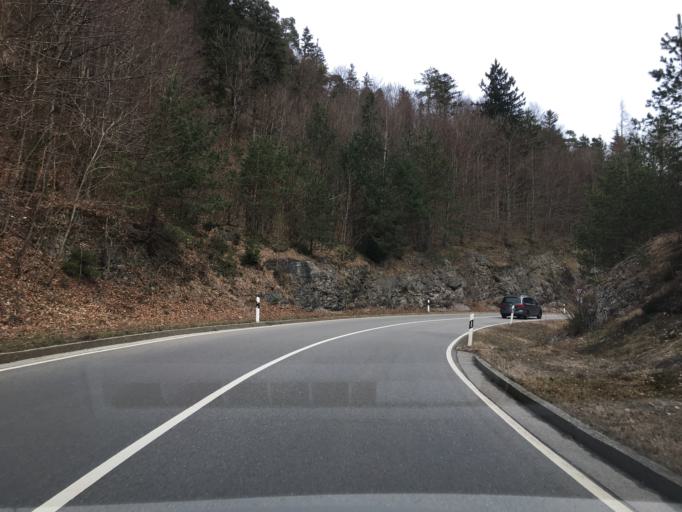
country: DE
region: Bavaria
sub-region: Upper Bavaria
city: Schneizlreuth
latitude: 47.7047
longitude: 12.8050
